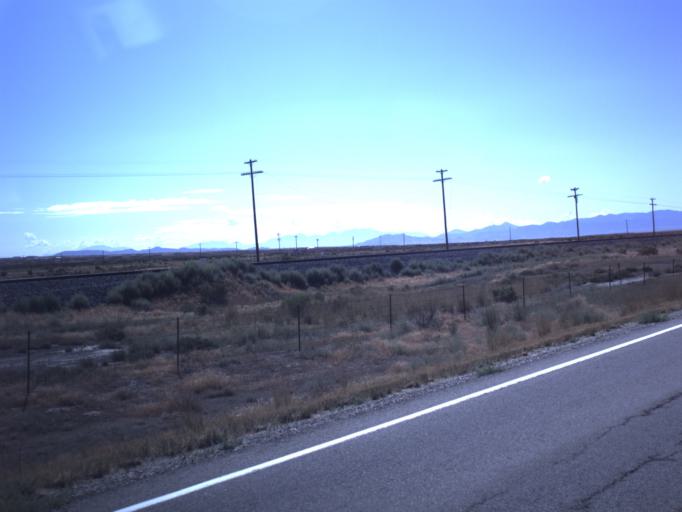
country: US
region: Utah
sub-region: Tooele County
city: Tooele
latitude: 40.3197
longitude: -112.4063
